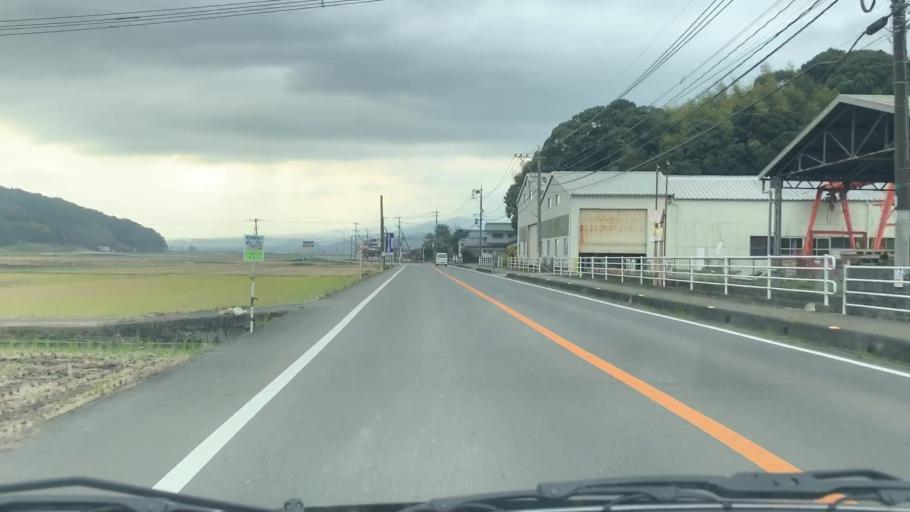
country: JP
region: Saga Prefecture
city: Kashima
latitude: 33.1462
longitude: 130.0630
